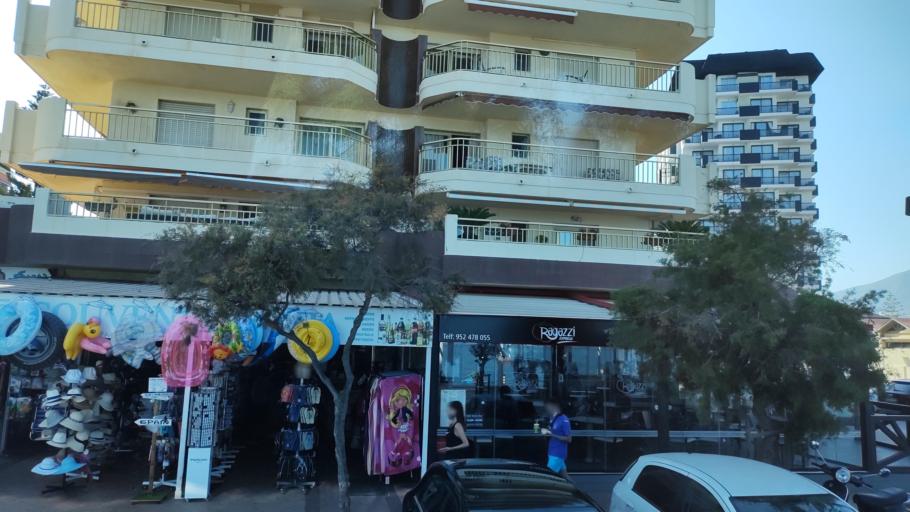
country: ES
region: Andalusia
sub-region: Provincia de Malaga
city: Fuengirola
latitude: 36.5310
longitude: -4.6246
